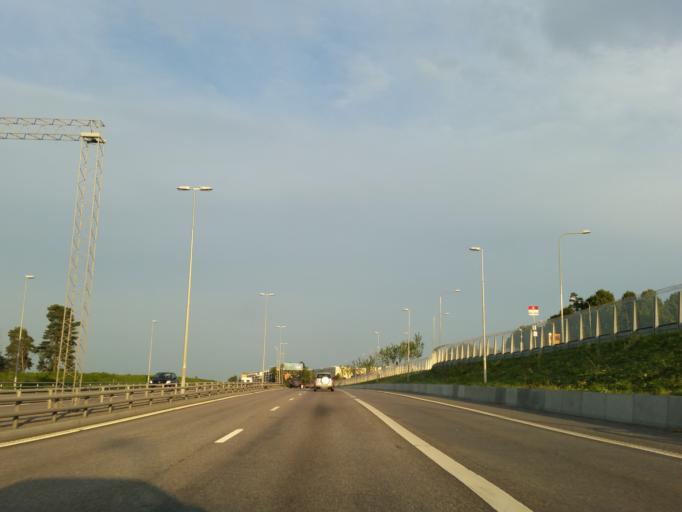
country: SE
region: Stockholm
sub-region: Stockholms Kommun
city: Kista
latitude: 59.3962
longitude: 17.9149
